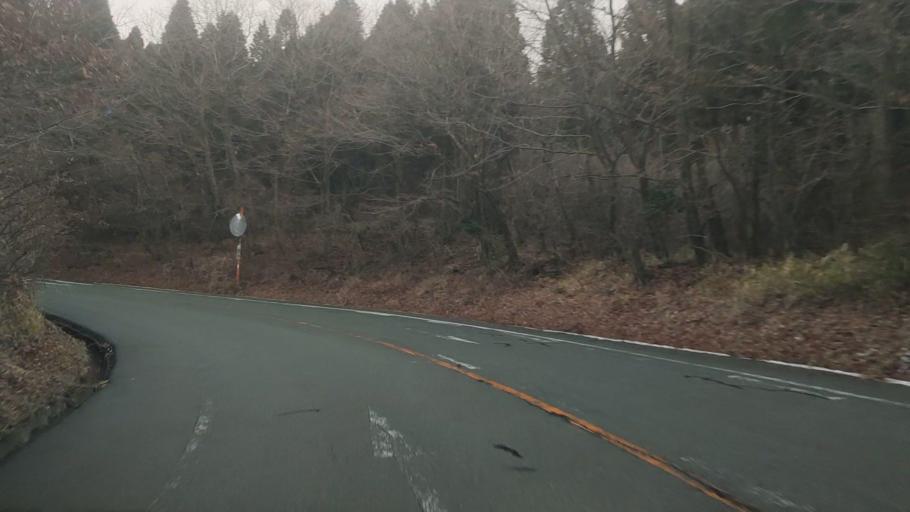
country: JP
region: Kumamoto
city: Aso
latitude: 32.8977
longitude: 131.0456
